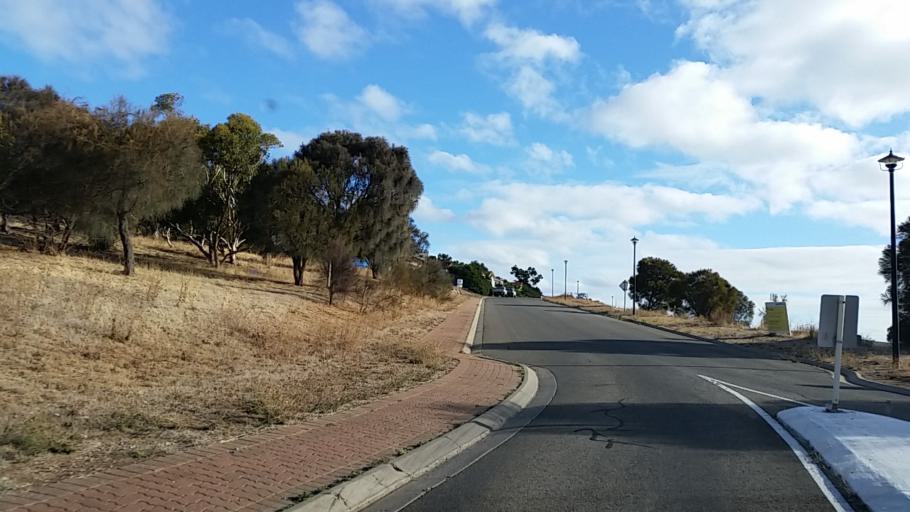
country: AU
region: South Australia
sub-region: Yankalilla
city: Normanville
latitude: -35.5015
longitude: 138.2503
